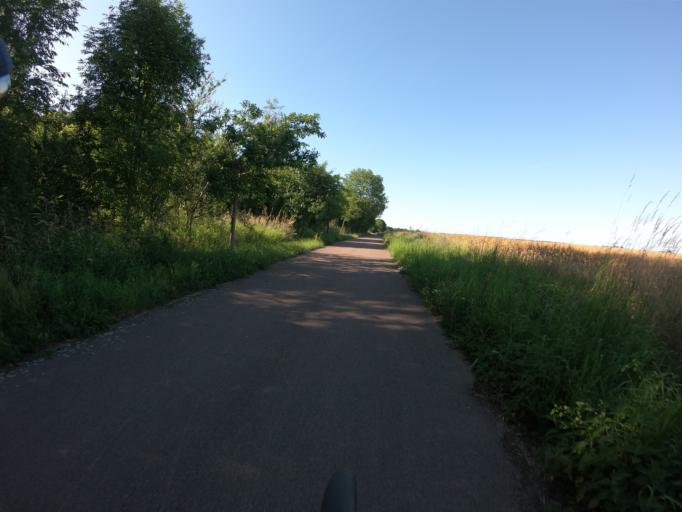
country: DE
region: Brandenburg
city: Juterbog
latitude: 52.0204
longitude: 13.0609
